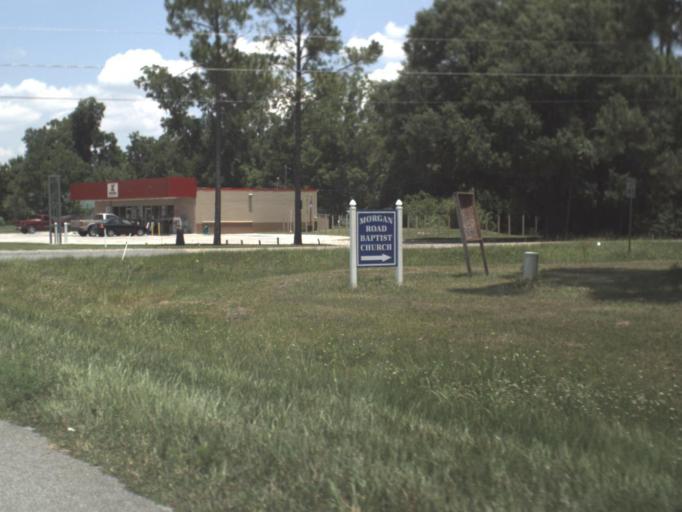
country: US
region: Florida
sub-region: Bradford County
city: Starke
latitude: 29.9969
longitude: -82.1325
